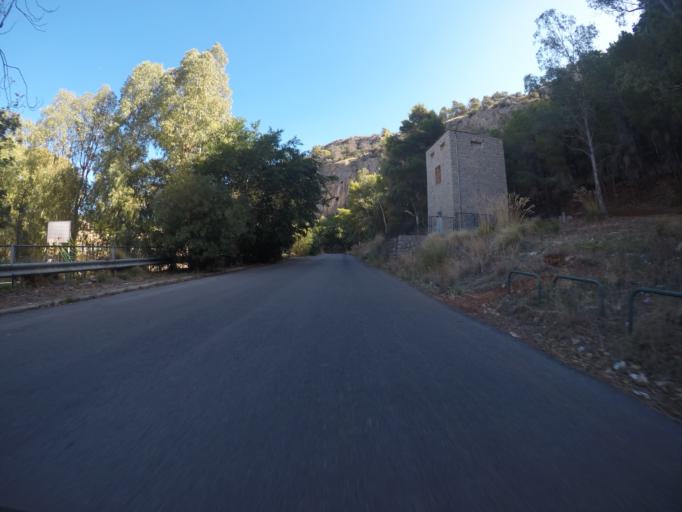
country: IT
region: Sicily
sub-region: Palermo
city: Palermo
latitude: 38.1904
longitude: 13.3359
